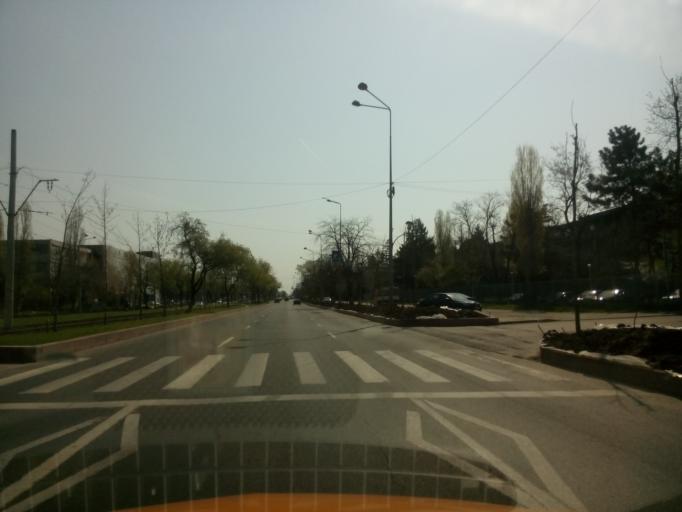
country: RO
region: Ilfov
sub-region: Comuna Glina
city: Catelu
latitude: 44.4083
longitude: 26.1890
